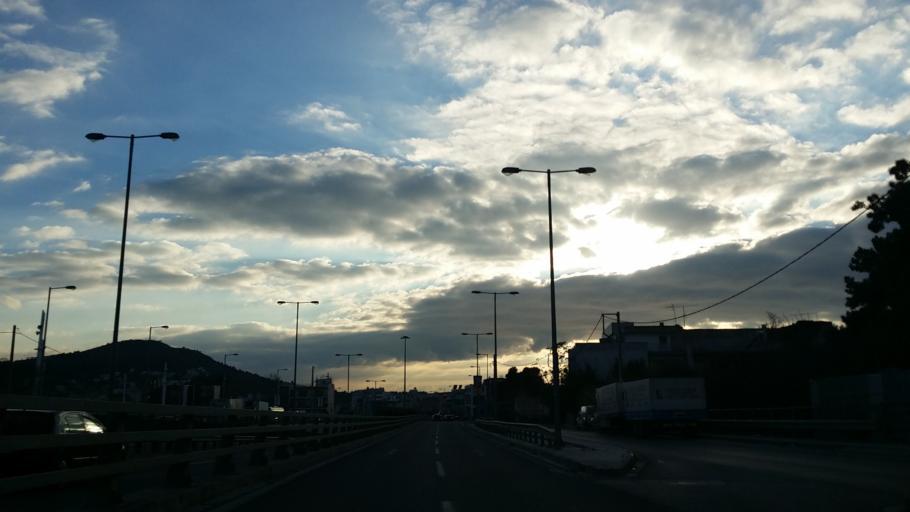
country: GR
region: Attica
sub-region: Nomarchia Athinas
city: Irakleio
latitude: 38.0422
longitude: 23.7784
